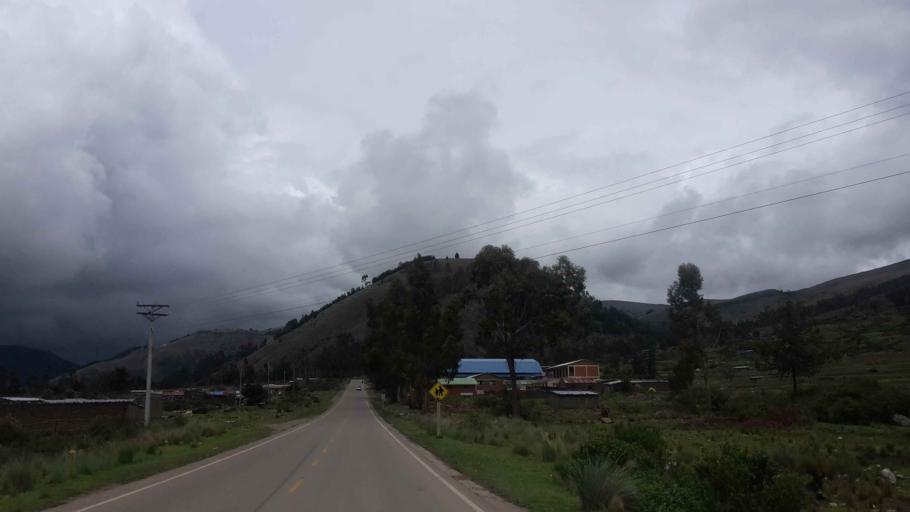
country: BO
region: Cochabamba
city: Arani
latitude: -17.4772
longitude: -65.5198
